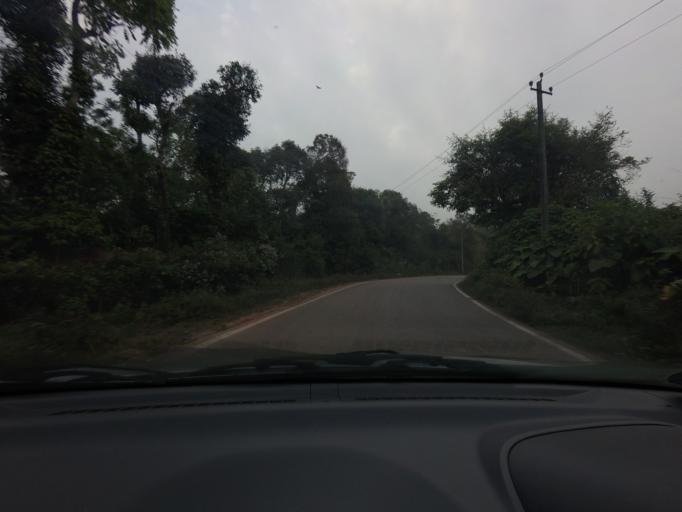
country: IN
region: Karnataka
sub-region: Hassan
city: Sakleshpur
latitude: 12.9113
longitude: 75.7519
